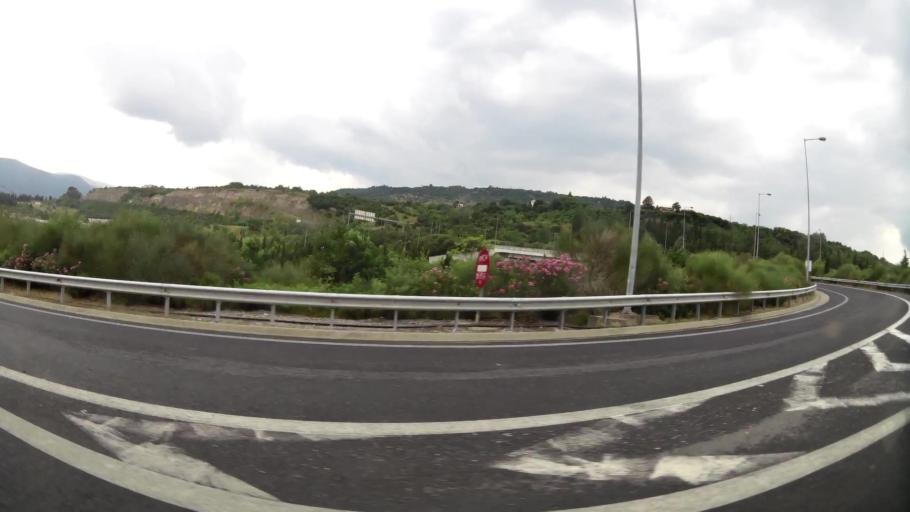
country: GR
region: Central Macedonia
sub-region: Nomos Imathias
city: Veroia
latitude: 40.5061
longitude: 22.2304
